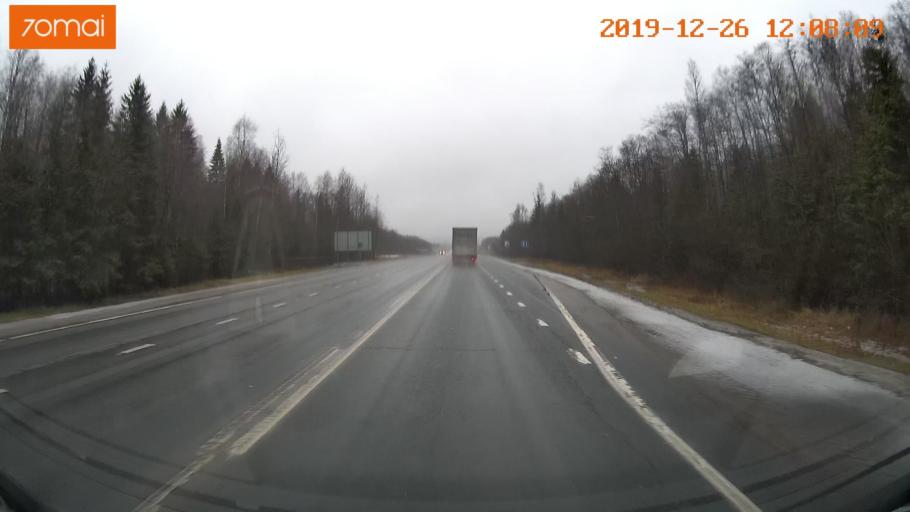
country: RU
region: Vologda
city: Tonshalovo
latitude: 59.2850
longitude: 38.0188
